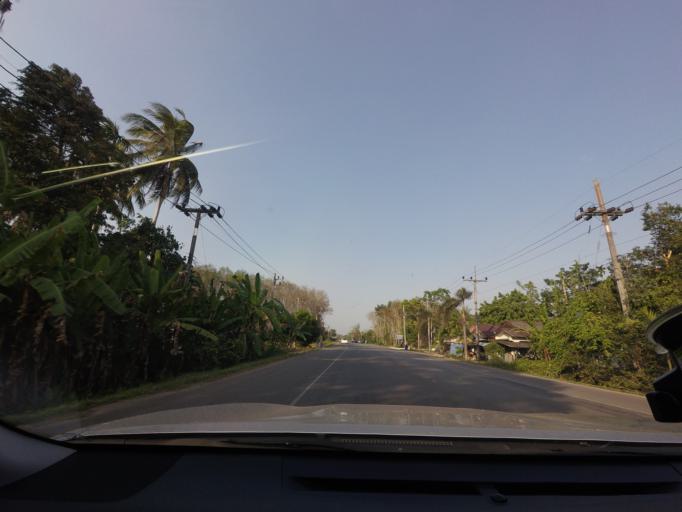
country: TH
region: Surat Thani
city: Phrasaeng
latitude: 8.5709
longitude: 99.2728
